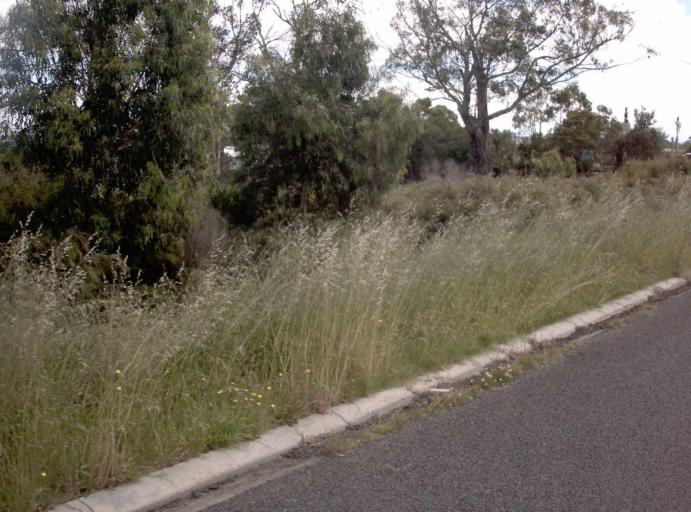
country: AU
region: Victoria
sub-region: Bass Coast
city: North Wonthaggi
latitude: -38.4193
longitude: 145.5203
